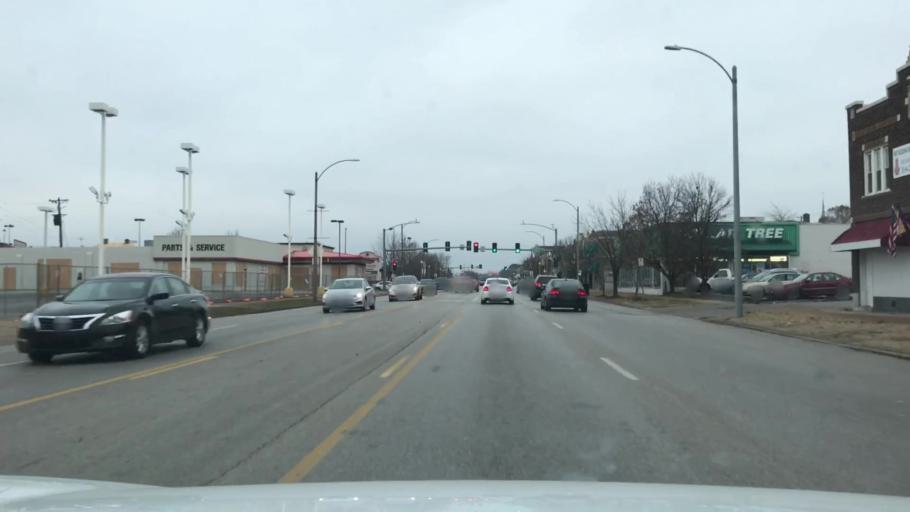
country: US
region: Missouri
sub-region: Saint Louis County
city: Maplewood
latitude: 38.5939
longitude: -90.2717
